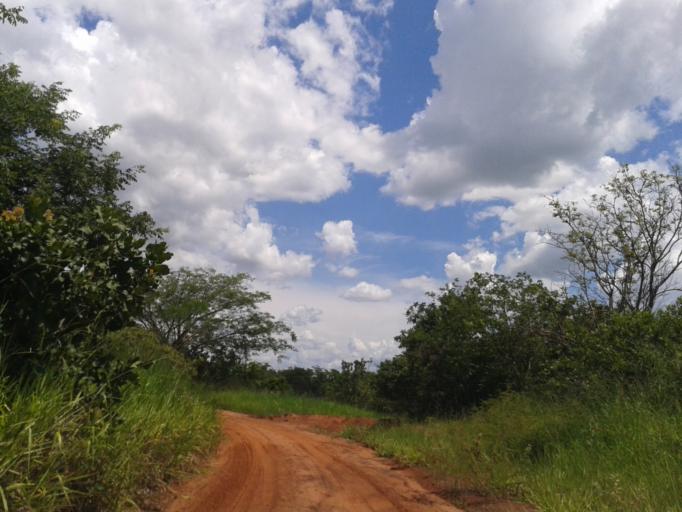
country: BR
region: Minas Gerais
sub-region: Ituiutaba
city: Ituiutaba
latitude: -18.8532
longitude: -49.5010
